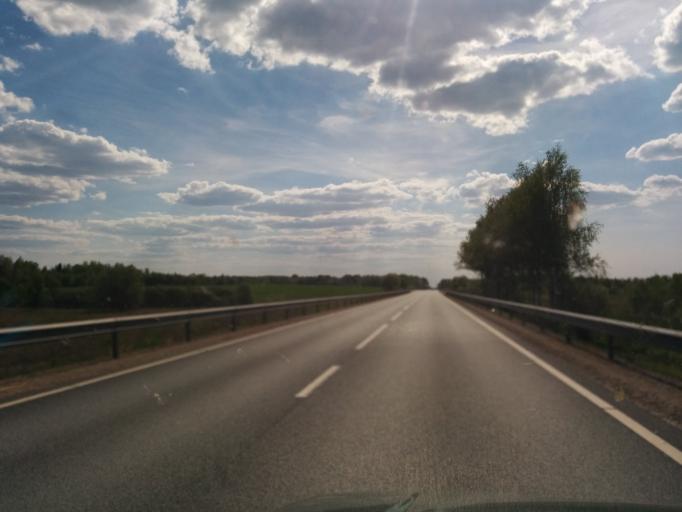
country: LV
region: Sigulda
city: Sigulda
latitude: 57.2411
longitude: 24.8339
